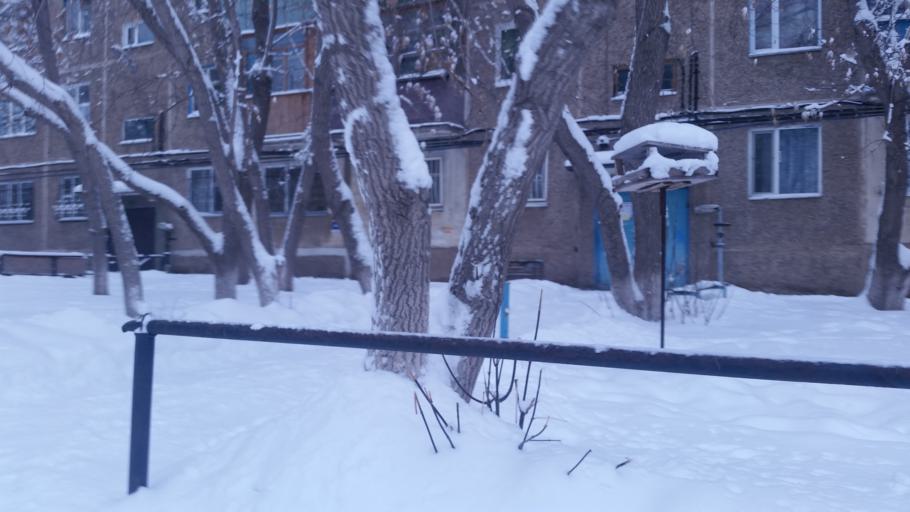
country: KZ
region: Qaraghandy
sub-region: Qaraghandy Qalasy
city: Karagandy
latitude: 49.7705
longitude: 73.1508
